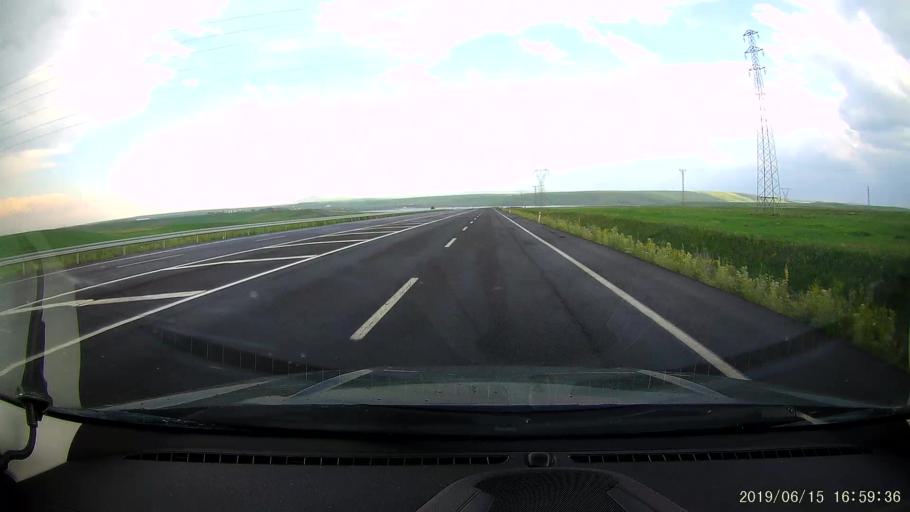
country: TR
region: Kars
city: Susuz
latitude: 40.7496
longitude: 43.1519
